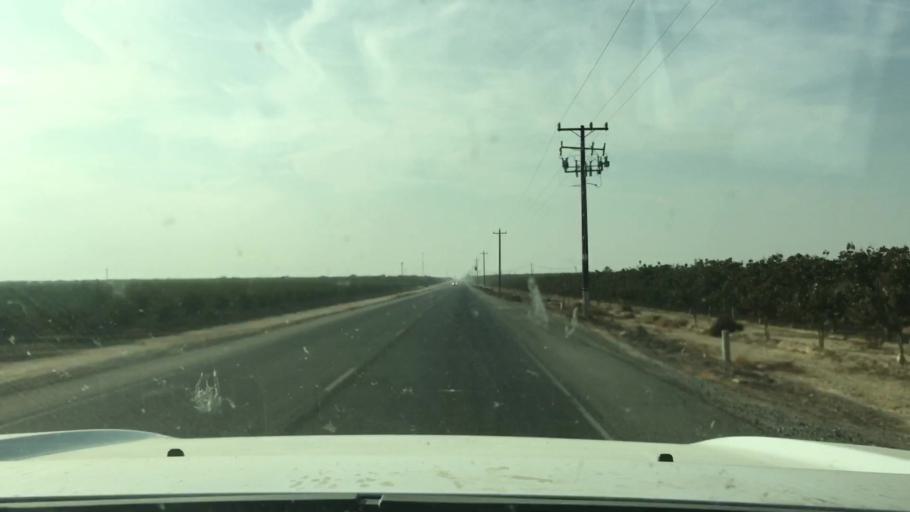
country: US
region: California
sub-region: Kern County
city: Buttonwillow
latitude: 35.5005
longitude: -119.4794
